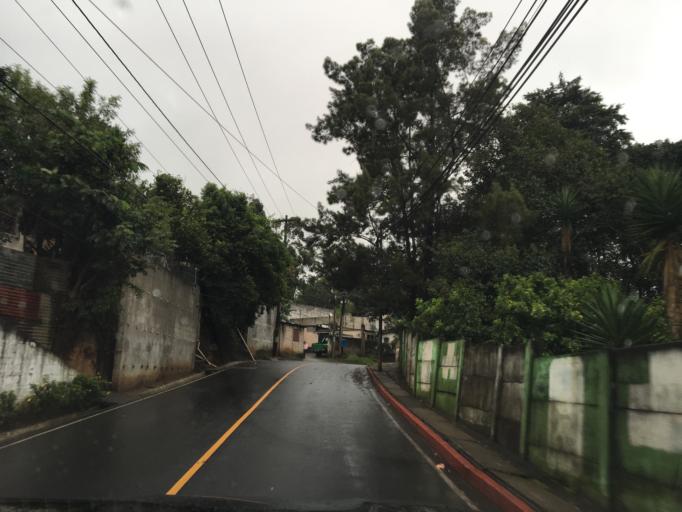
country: GT
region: Guatemala
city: Santa Catarina Pinula
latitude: 14.5608
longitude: -90.4996
